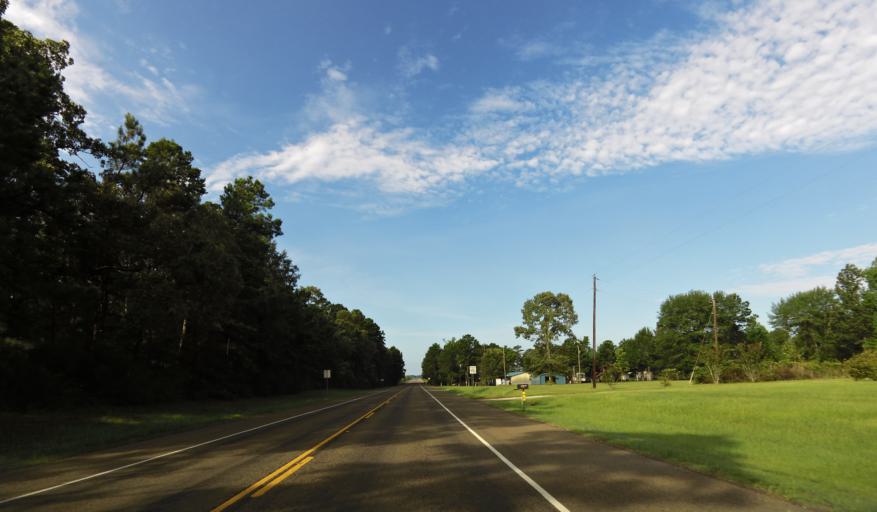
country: US
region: Texas
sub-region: Angelina County
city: Huntington
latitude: 31.2471
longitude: -94.3092
